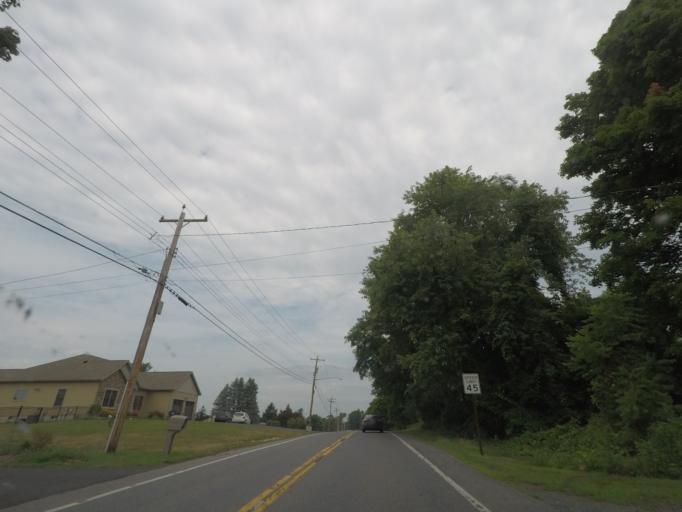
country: US
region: New York
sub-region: Saratoga County
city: Waterford
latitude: 42.8210
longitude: -73.7033
